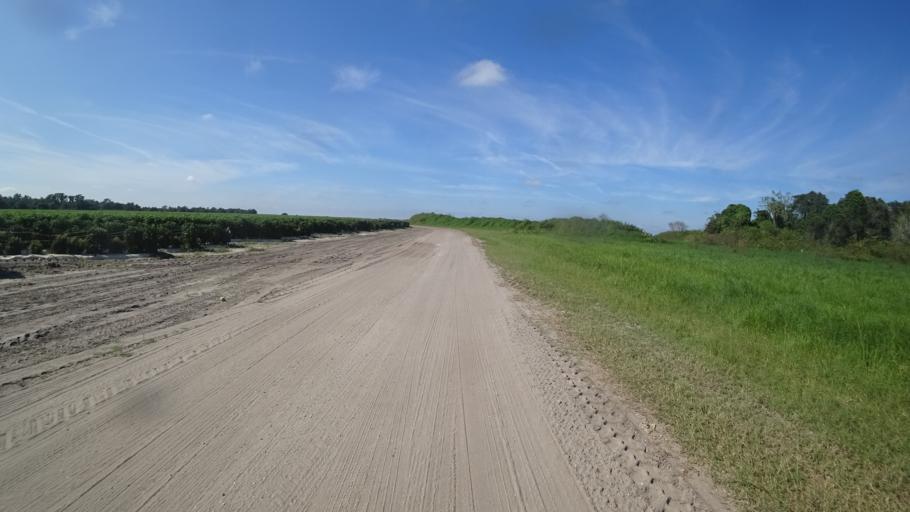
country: US
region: Florida
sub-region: DeSoto County
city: Arcadia
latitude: 27.2942
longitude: -82.0444
